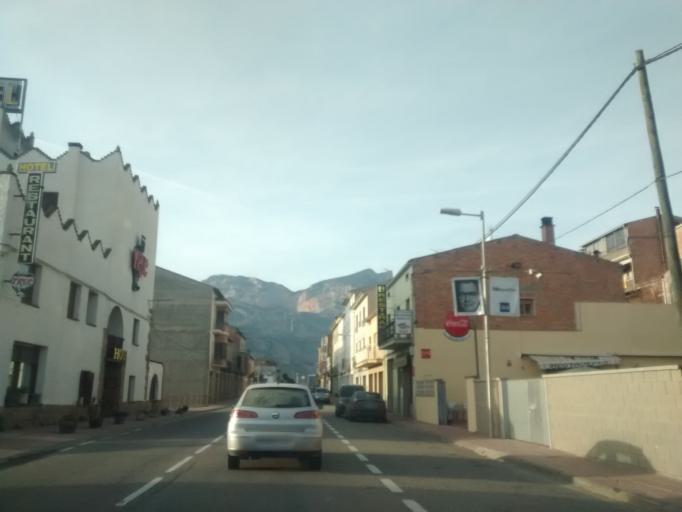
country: ES
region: Catalonia
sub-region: Provincia de Lleida
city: Oliana
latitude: 42.0704
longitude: 1.3122
